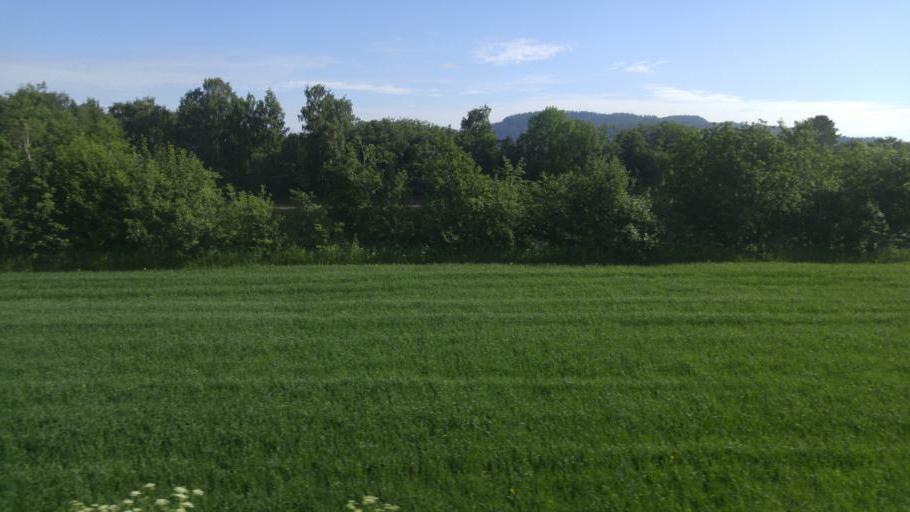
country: NO
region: Nord-Trondelag
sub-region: Stjordal
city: Stjordalshalsen
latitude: 63.4456
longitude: 10.9648
